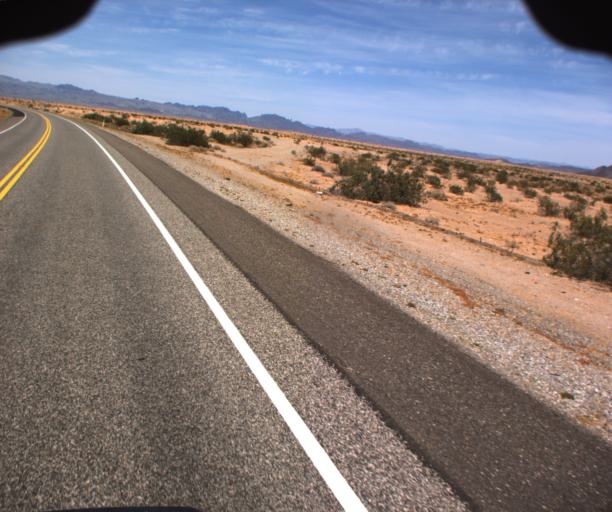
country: US
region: Arizona
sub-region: La Paz County
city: Parker
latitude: 34.0678
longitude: -114.2583
